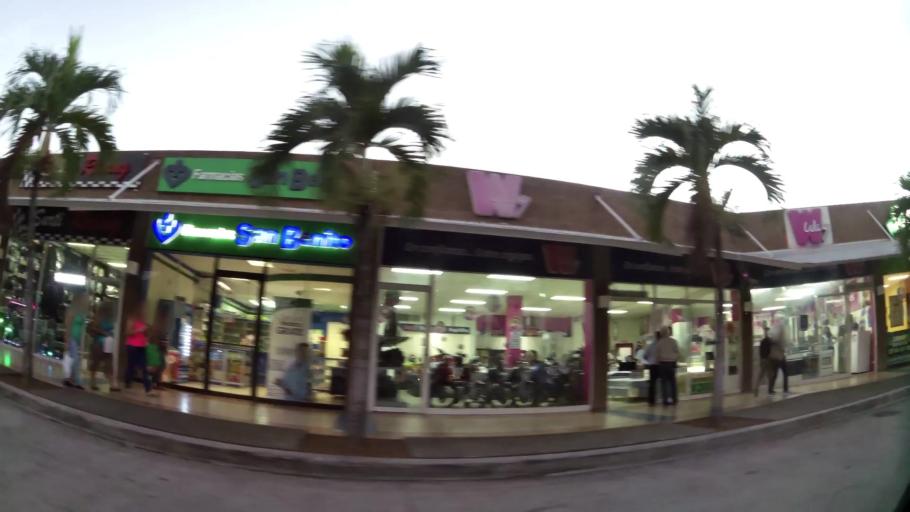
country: SV
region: La Libertad
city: Santa Tecla
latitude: 13.7281
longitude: -89.3594
